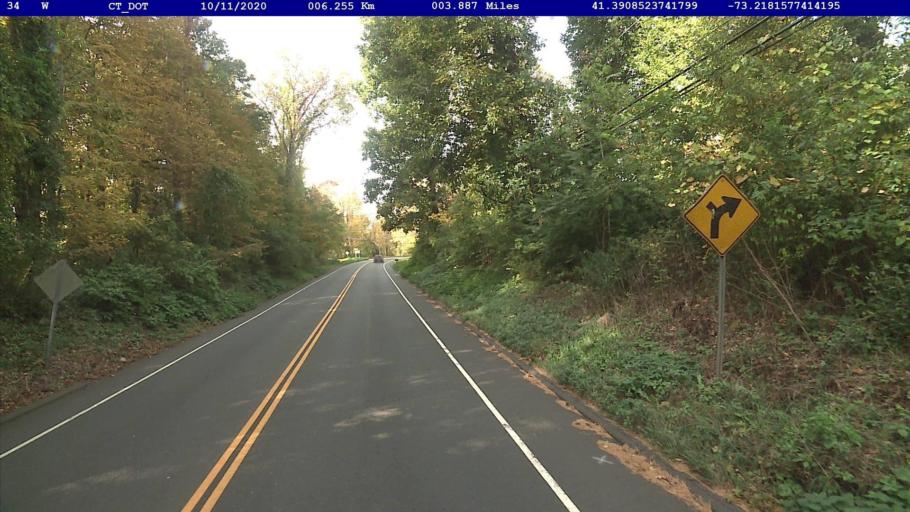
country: US
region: Connecticut
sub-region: Fairfield County
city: Newtown
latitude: 41.3906
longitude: -73.2179
